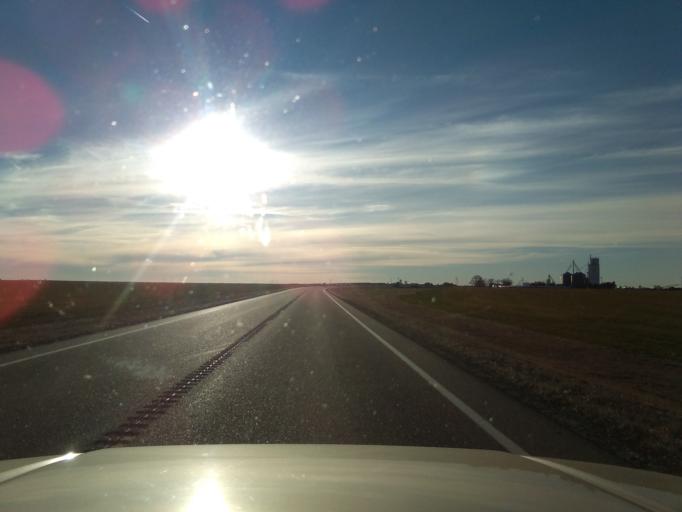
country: US
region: Kansas
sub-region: Thomas County
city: Colby
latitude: 39.4506
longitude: -100.8065
